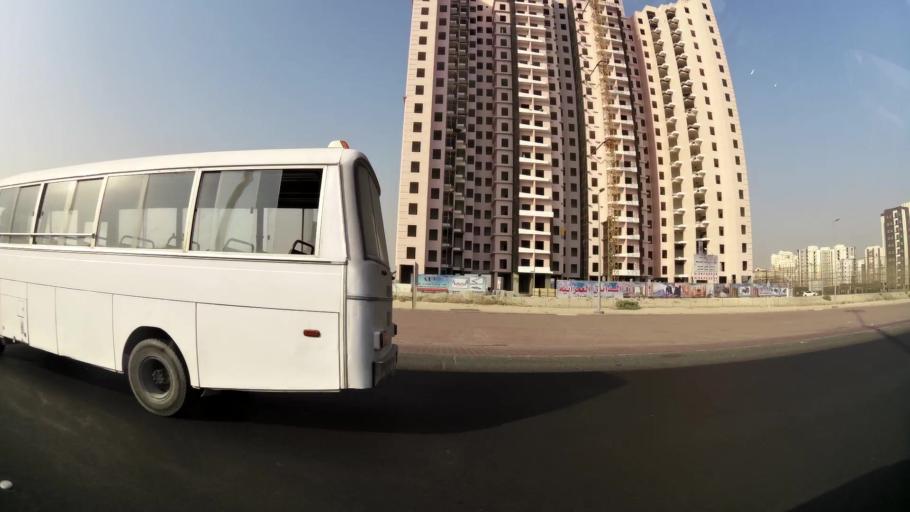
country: KW
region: Mubarak al Kabir
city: Sabah as Salim
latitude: 29.2608
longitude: 48.0873
